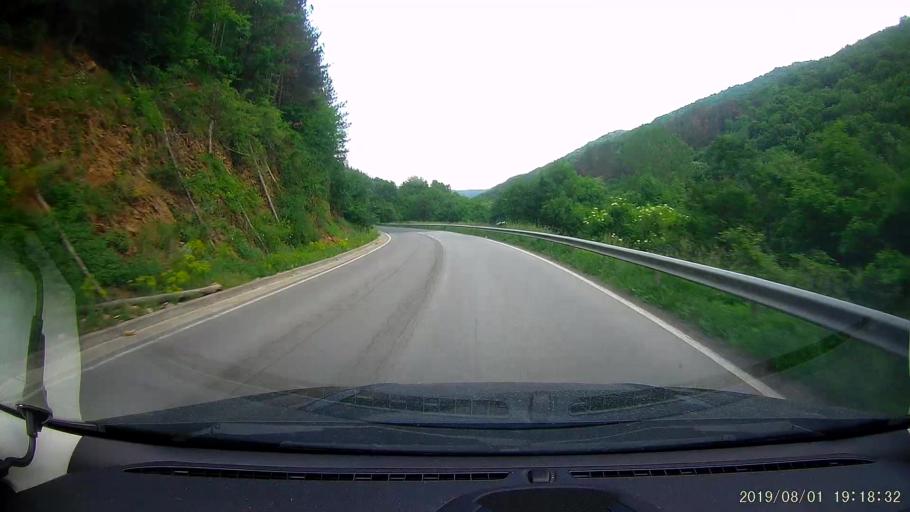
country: BG
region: Shumen
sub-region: Obshtina Smyadovo
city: Smyadovo
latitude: 42.9118
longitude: 26.9397
